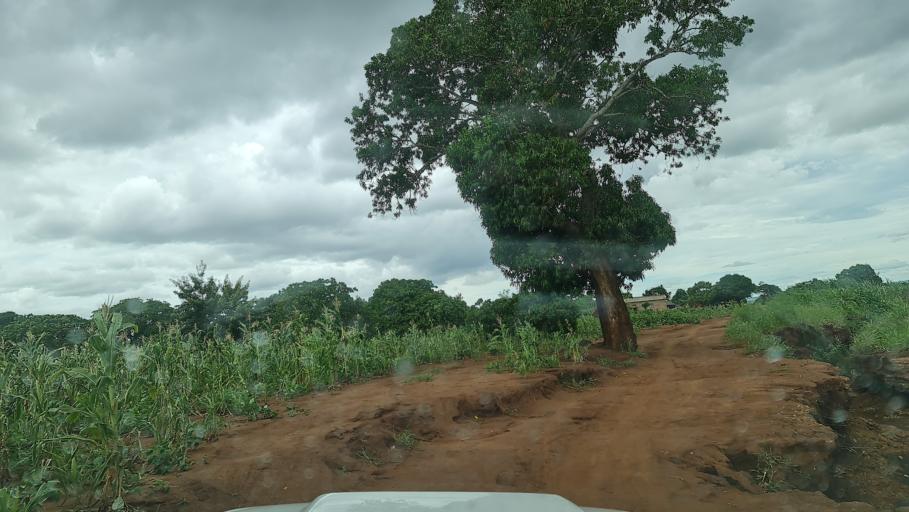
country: MZ
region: Nampula
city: Nacala
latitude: -14.7493
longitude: 40.0251
